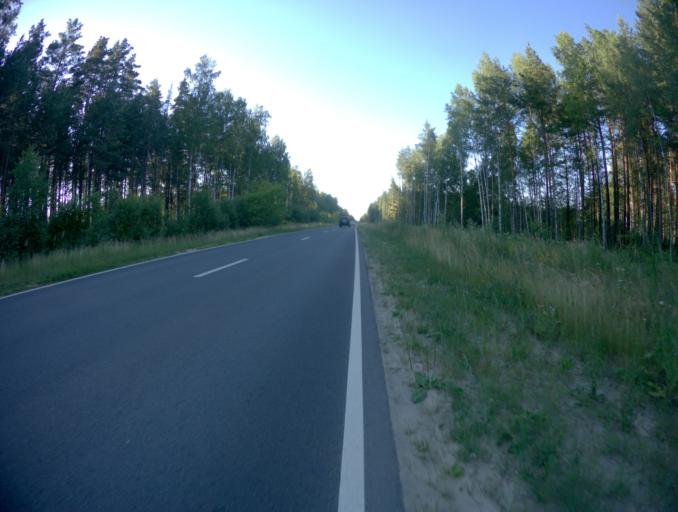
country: RU
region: Vladimir
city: Galitsy
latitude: 56.0692
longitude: 42.8668
